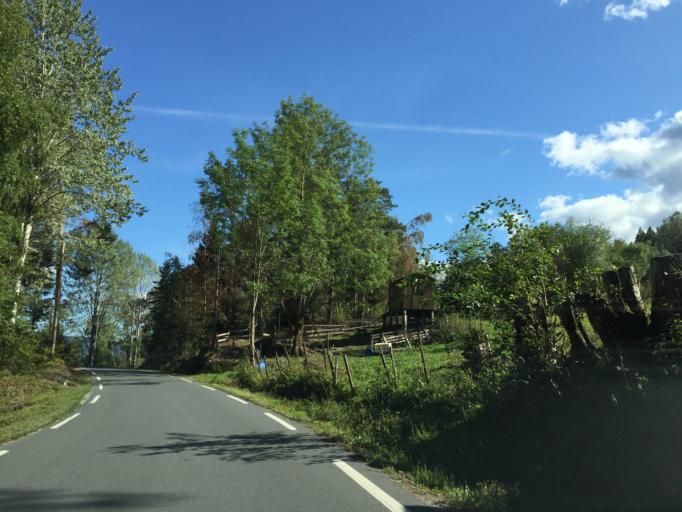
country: NO
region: Buskerud
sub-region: Ovre Eiker
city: Hokksund
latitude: 59.6778
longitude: 9.8643
